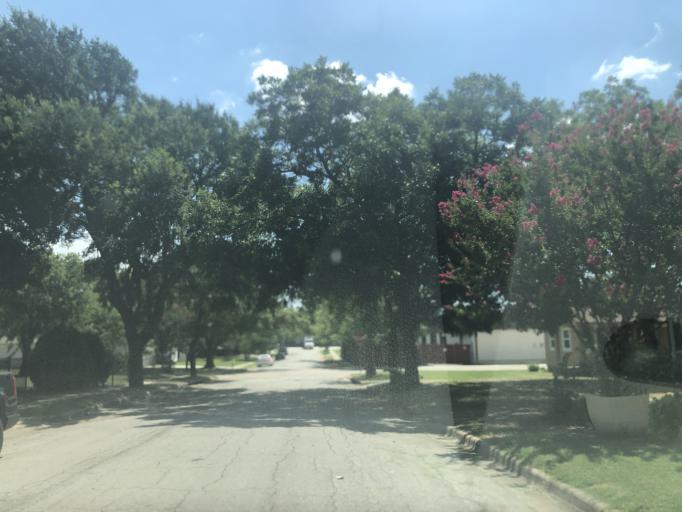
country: US
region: Texas
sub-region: Dallas County
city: Grand Prairie
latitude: 32.7421
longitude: -97.0279
